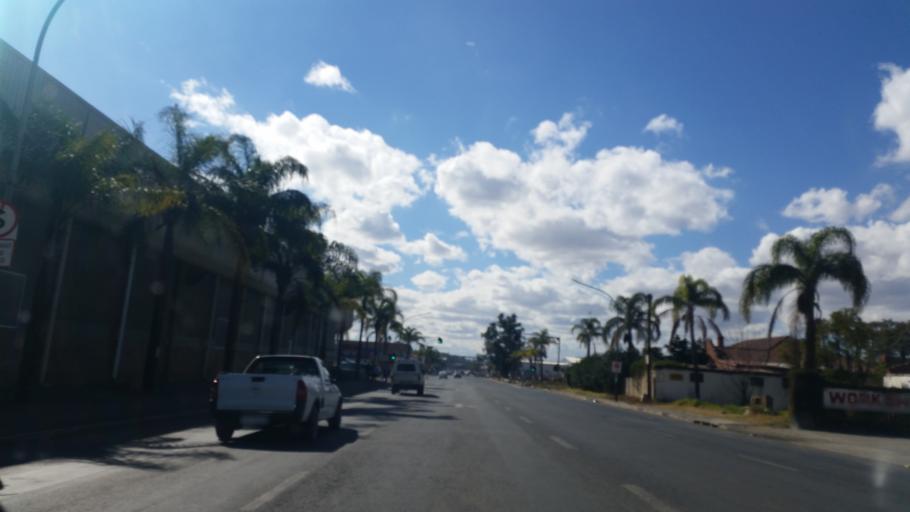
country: ZA
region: KwaZulu-Natal
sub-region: uThukela District Municipality
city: Ladysmith
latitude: -28.5639
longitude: 29.7804
